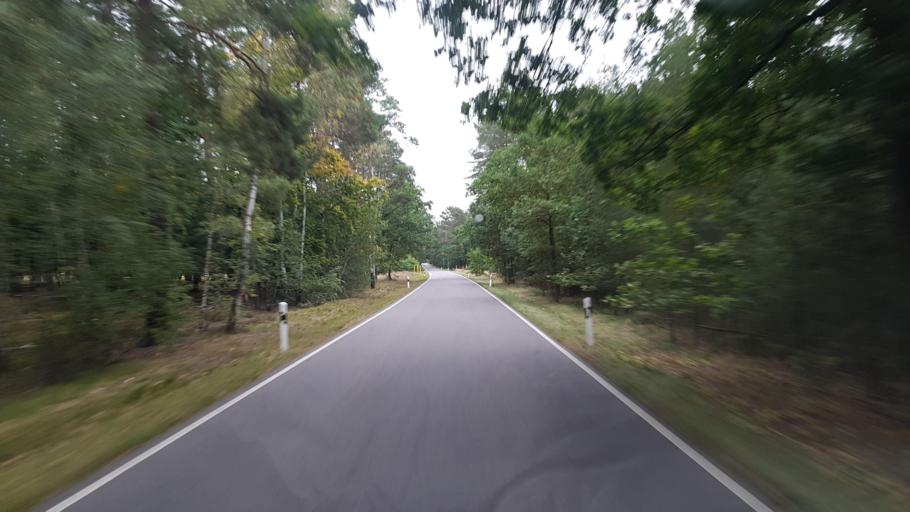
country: DE
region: Brandenburg
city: Luckau
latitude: 51.8819
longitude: 13.6755
